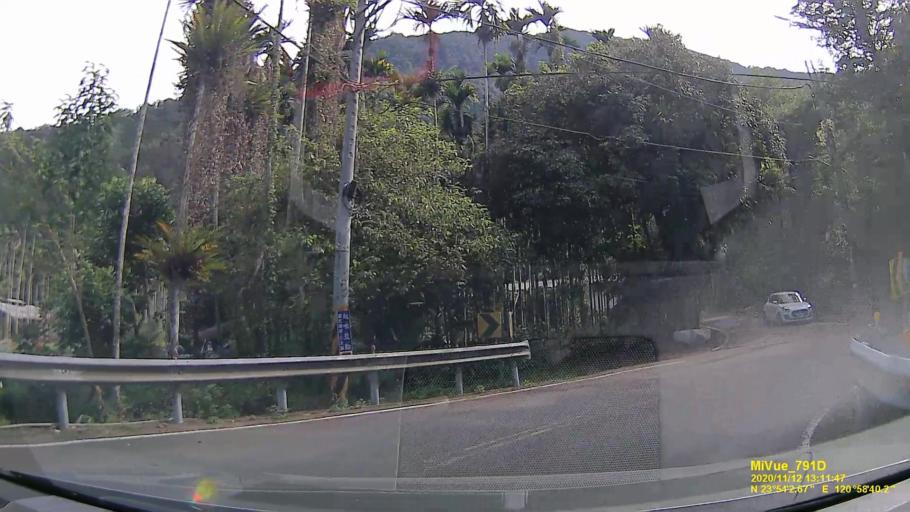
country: TW
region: Taiwan
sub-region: Nantou
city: Puli
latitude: 23.9007
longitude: 120.9779
